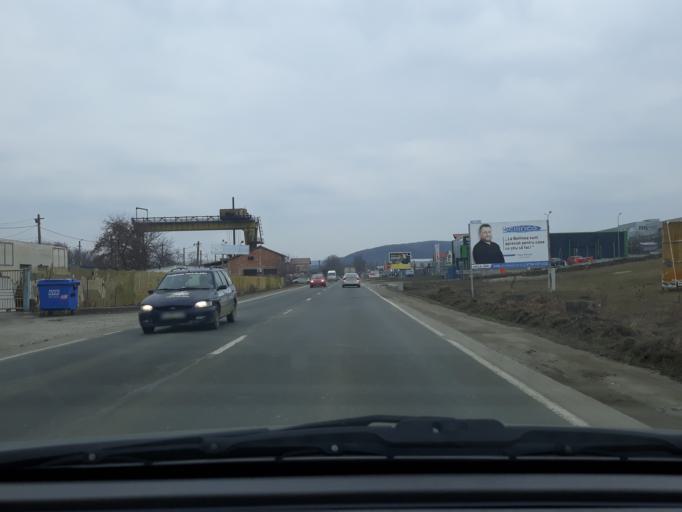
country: RO
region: Salaj
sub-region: Comuna Criseni
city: Criseni
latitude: 47.2239
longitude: 23.0286
